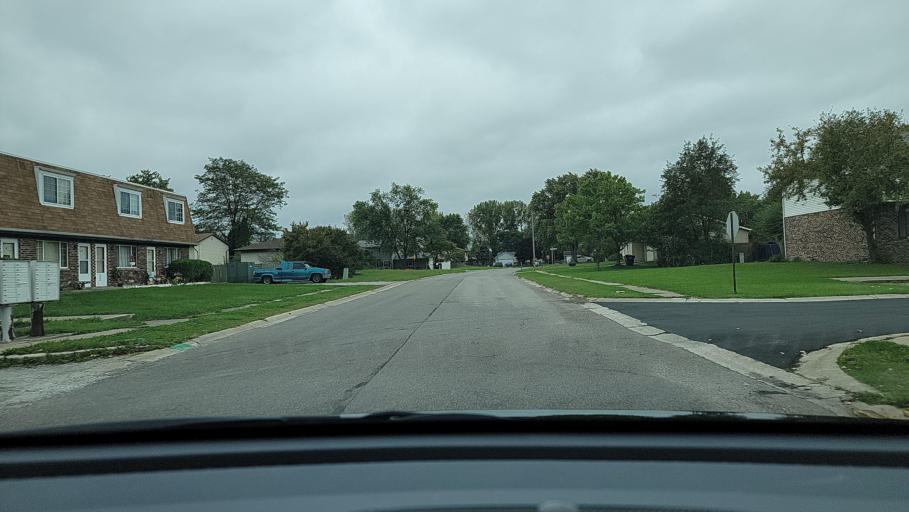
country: US
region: Indiana
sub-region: Porter County
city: Portage
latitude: 41.5480
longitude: -87.1882
